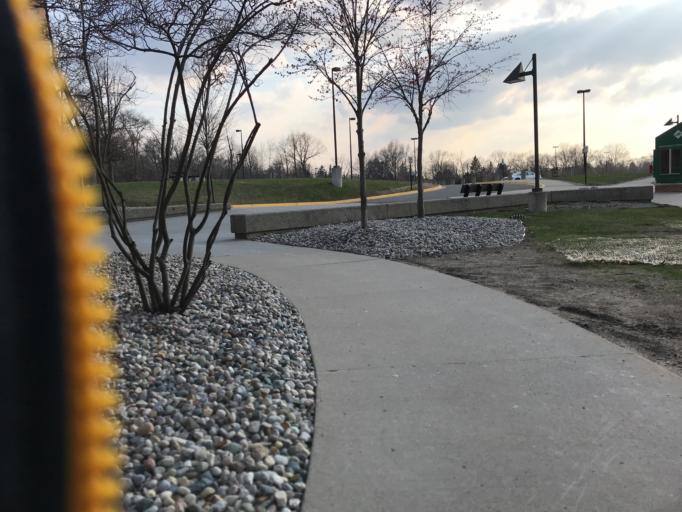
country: US
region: Michigan
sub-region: Oakland County
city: Farmington Hills
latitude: 42.4927
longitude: -83.3727
